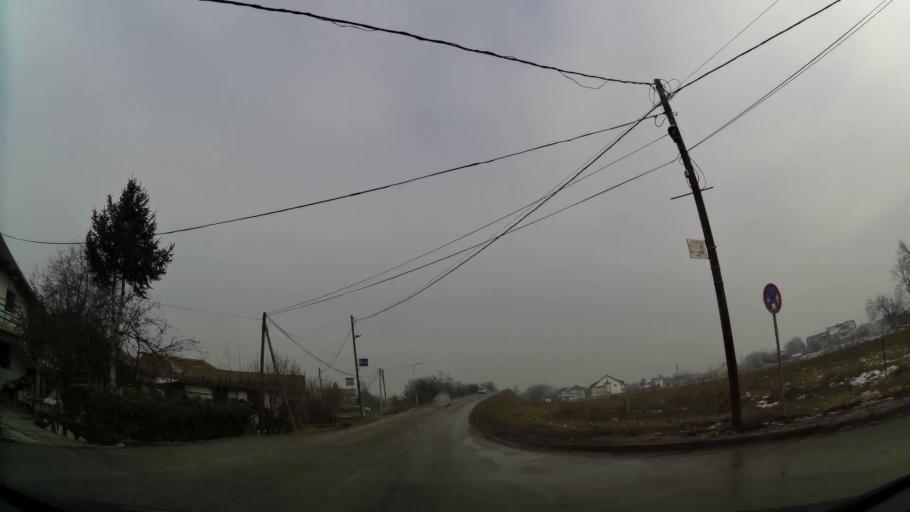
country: MK
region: Ilinden
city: Ilinden
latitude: 41.9952
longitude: 21.5578
